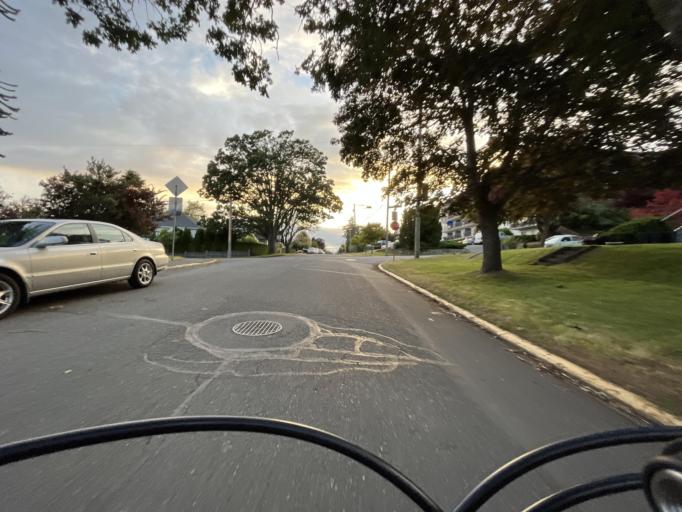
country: CA
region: British Columbia
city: Victoria
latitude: 48.4284
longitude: -123.4035
